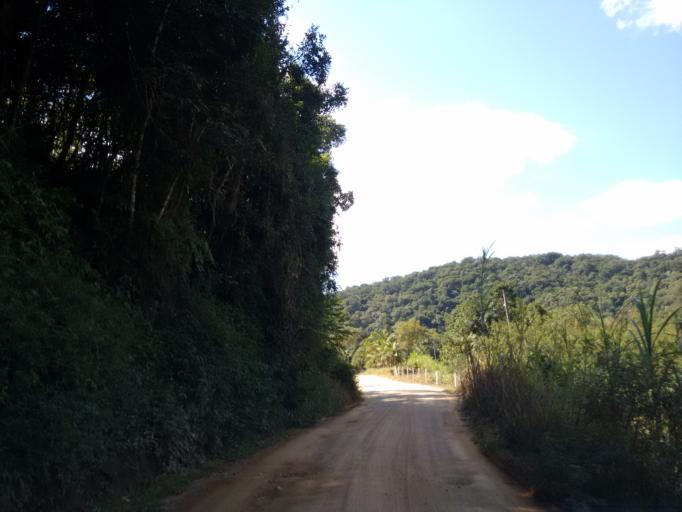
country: BR
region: Santa Catarina
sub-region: Indaial
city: Indaial
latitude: -26.9671
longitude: -49.1788
